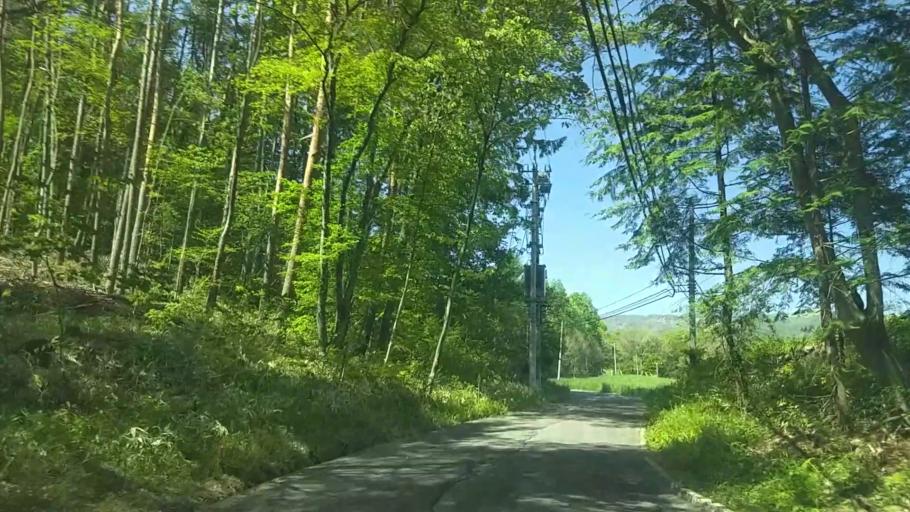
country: JP
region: Yamanashi
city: Nirasaki
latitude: 35.8925
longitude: 138.4378
